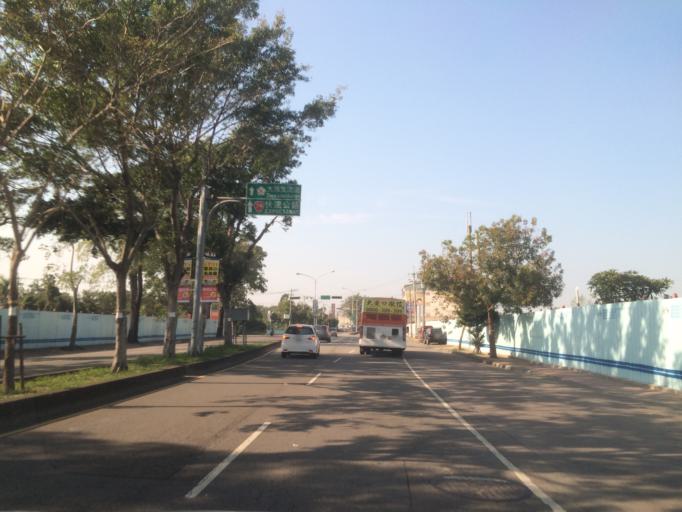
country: TW
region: Taiwan
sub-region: Taichung City
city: Taichung
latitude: 24.1833
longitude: 120.6792
